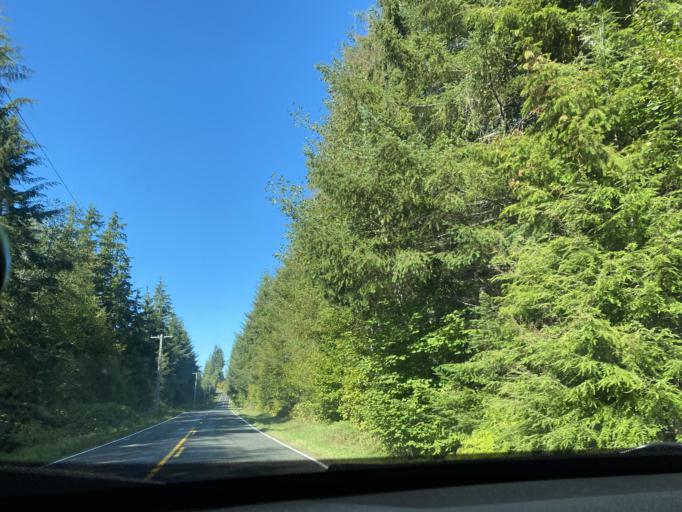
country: US
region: Washington
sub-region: Clallam County
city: Forks
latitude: 47.9476
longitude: -124.5005
